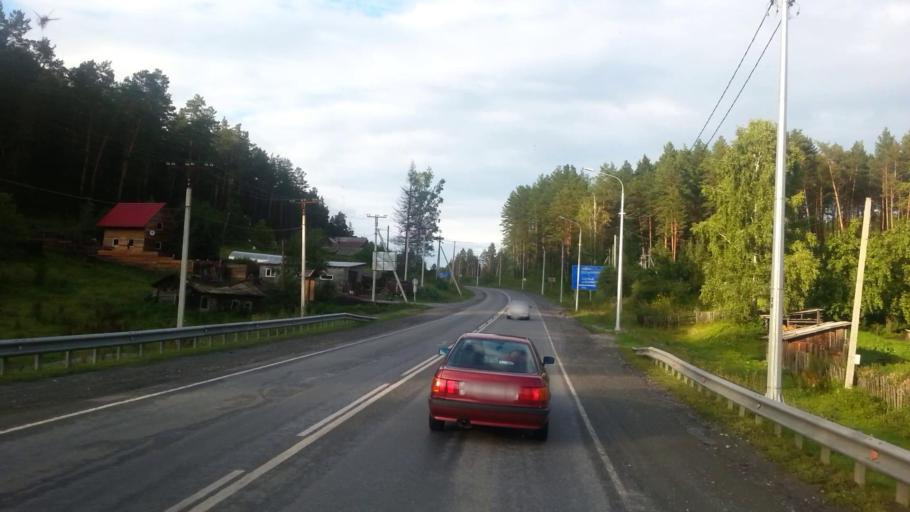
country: RU
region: Altay
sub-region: Mayminskiy Rayon
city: Manzherok
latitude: 51.8189
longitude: 85.7821
